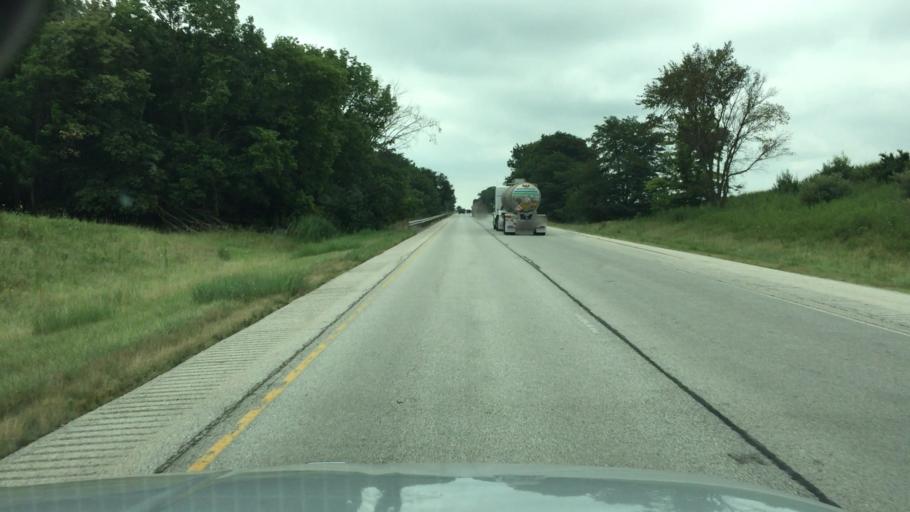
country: US
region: Illinois
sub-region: Knox County
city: Galesburg
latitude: 41.0697
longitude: -90.3345
